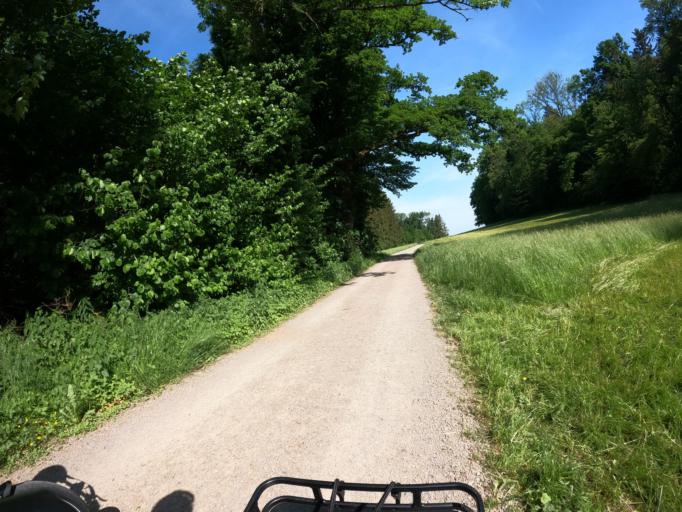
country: CH
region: Zurich
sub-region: Bezirk Dielsdorf
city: Niederglatt
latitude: 47.4887
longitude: 8.4911
